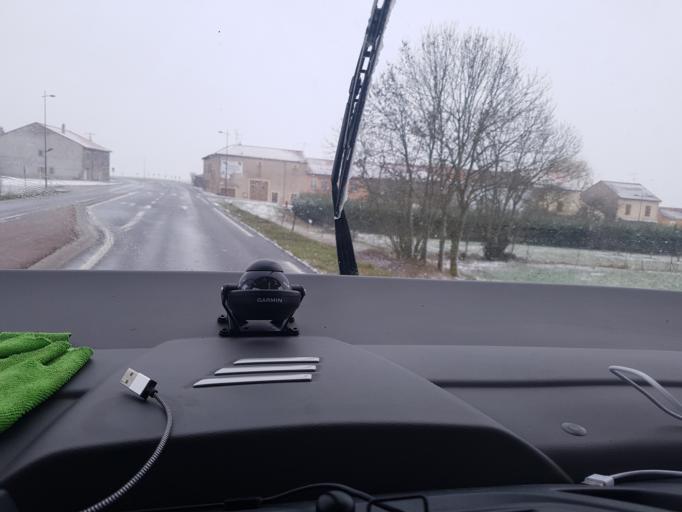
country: FR
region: Lorraine
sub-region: Departement de la Moselle
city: Solgne
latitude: 48.8922
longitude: 6.3655
